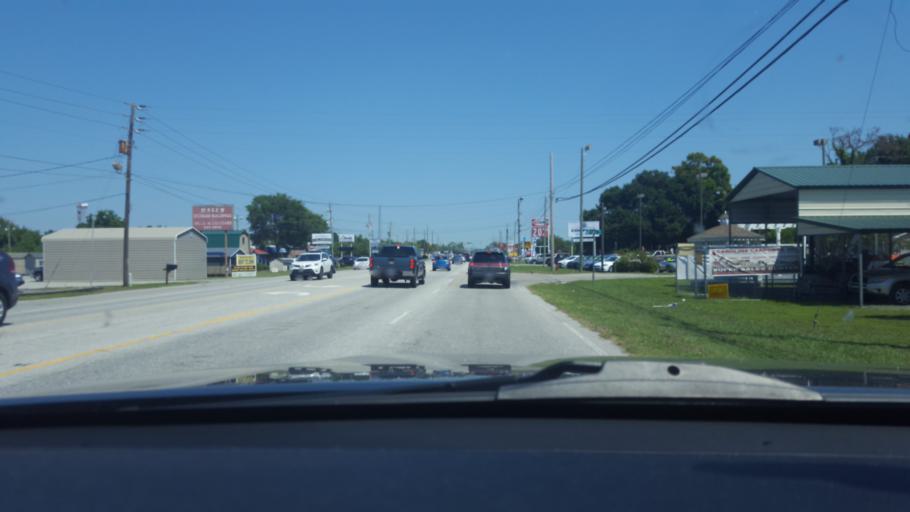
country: US
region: North Carolina
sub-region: New Hanover County
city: Kings Grant
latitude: 34.2539
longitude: -77.8478
